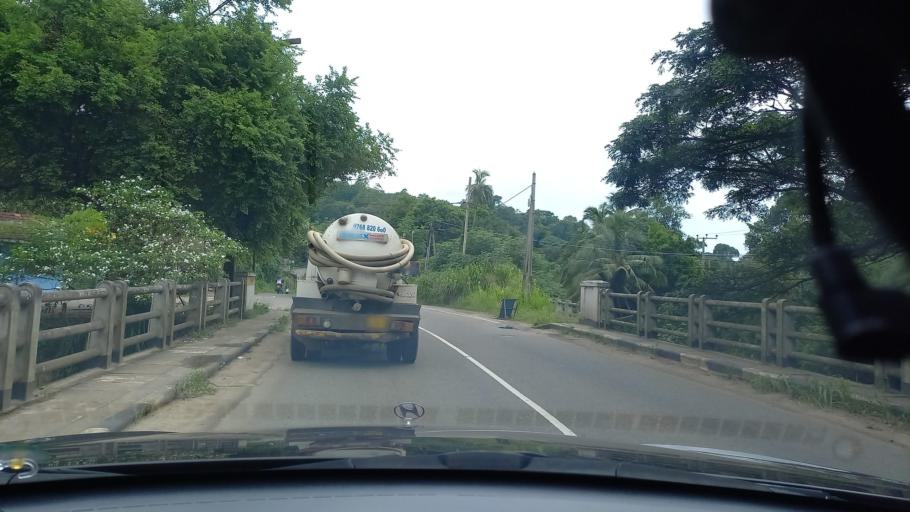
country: LK
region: Central
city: Kadugannawa
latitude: 7.2487
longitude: 80.4745
